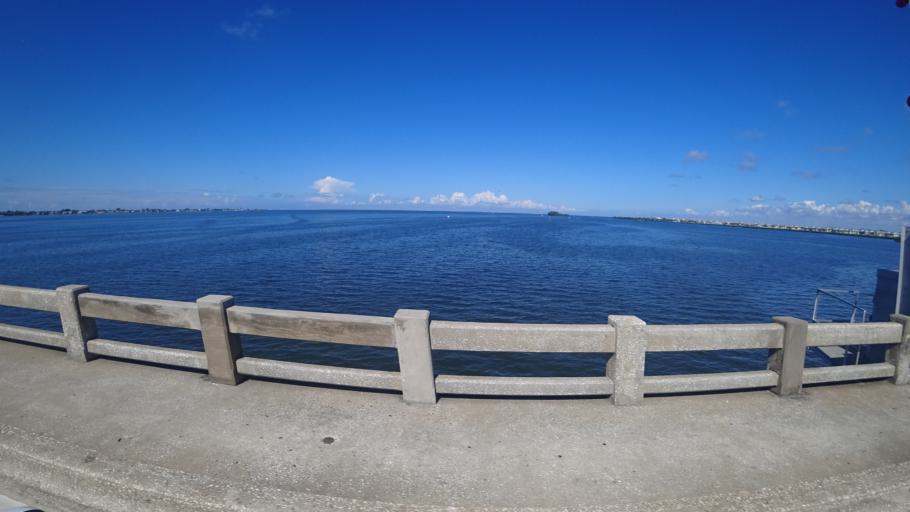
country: US
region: Florida
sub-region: Manatee County
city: Holmes Beach
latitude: 27.4970
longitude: -82.6938
